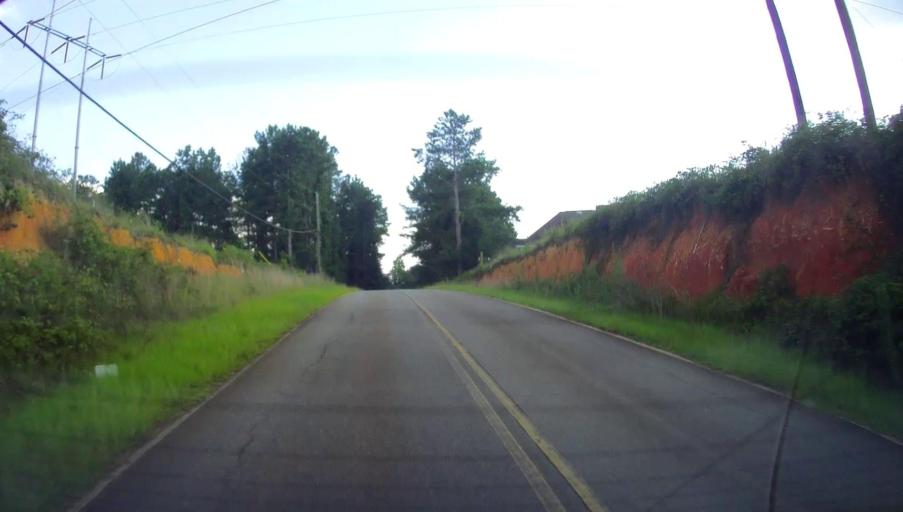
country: US
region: Georgia
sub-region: Houston County
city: Centerville
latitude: 32.5871
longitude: -83.6525
